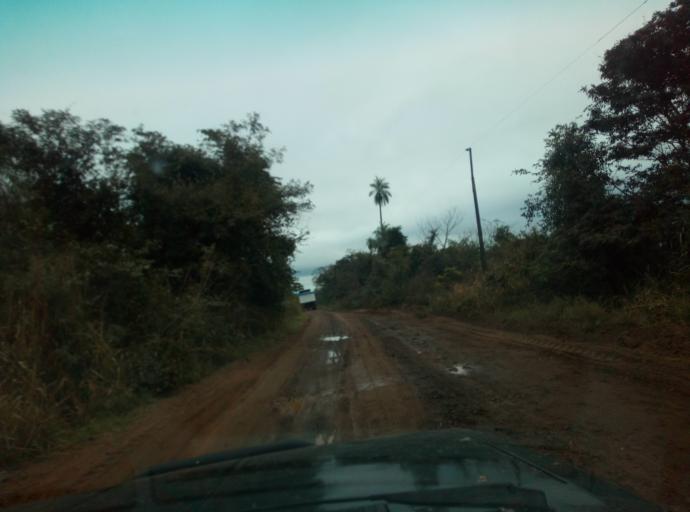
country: PY
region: Caaguazu
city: Carayao
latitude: -25.1902
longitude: -56.3797
